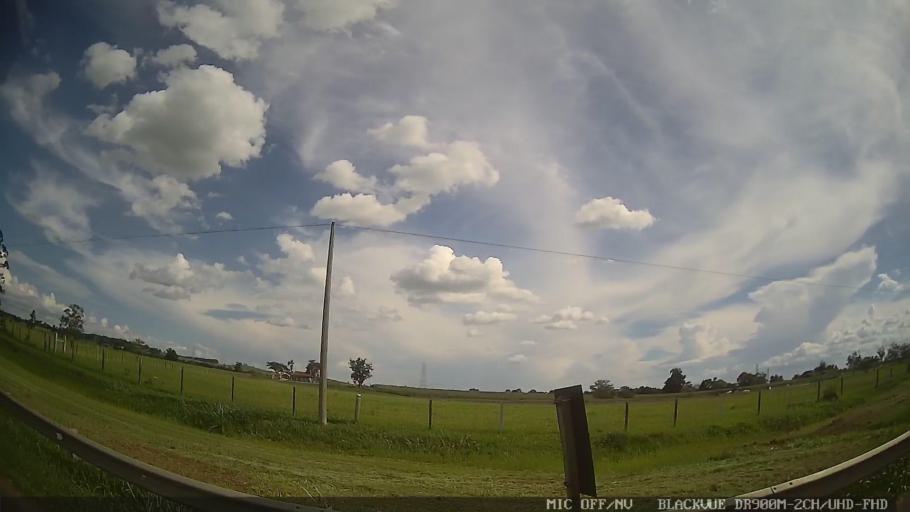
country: BR
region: Sao Paulo
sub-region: Conchas
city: Conchas
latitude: -23.0445
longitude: -47.9404
